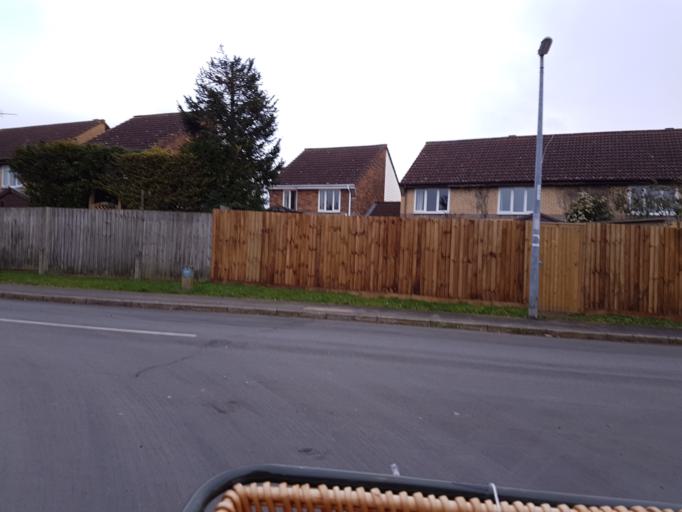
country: GB
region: England
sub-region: Cambridgeshire
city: Fulbourn
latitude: 52.1866
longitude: 0.1842
